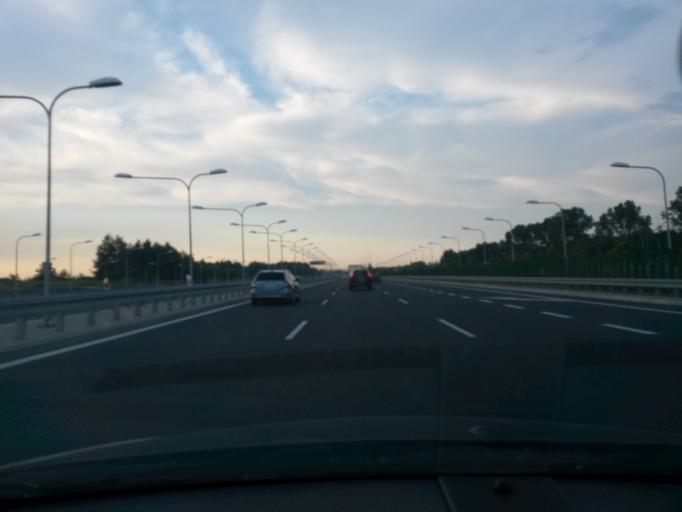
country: PL
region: Masovian Voivodeship
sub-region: Powiat pruszkowski
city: Rybie
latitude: 52.1453
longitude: 20.9886
